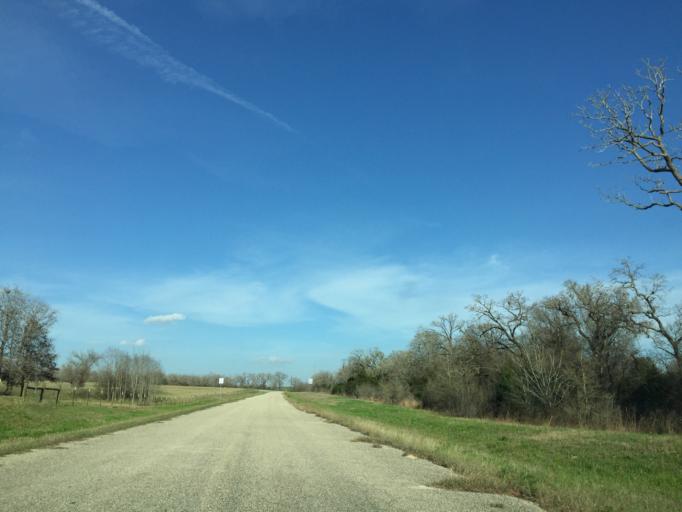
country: US
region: Texas
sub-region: Lee County
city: Lexington
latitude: 30.4603
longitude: -97.1505
